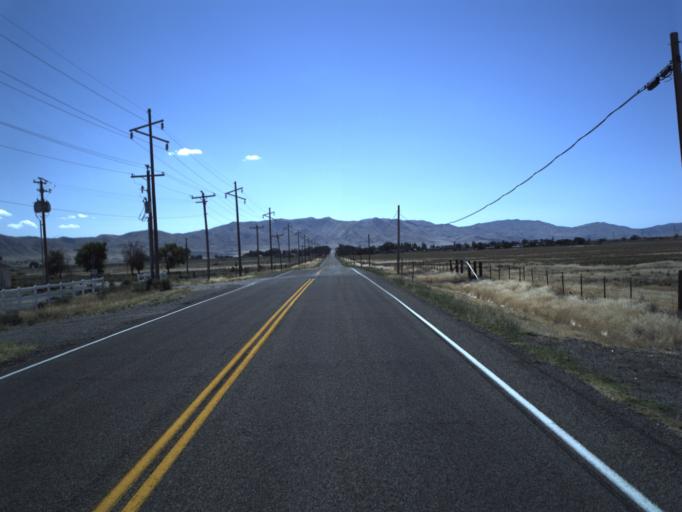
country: US
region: Utah
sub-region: Utah County
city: Genola
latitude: 39.9744
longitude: -111.9569
